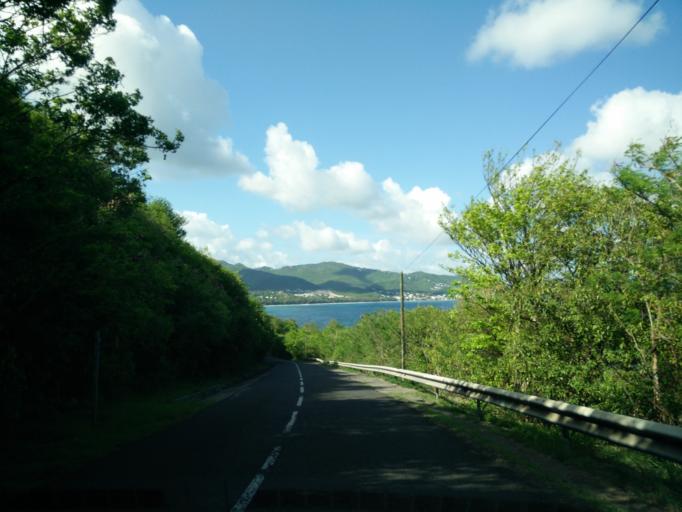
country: MQ
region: Martinique
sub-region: Martinique
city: Les Trois-Ilets
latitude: 14.4587
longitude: -61.0490
